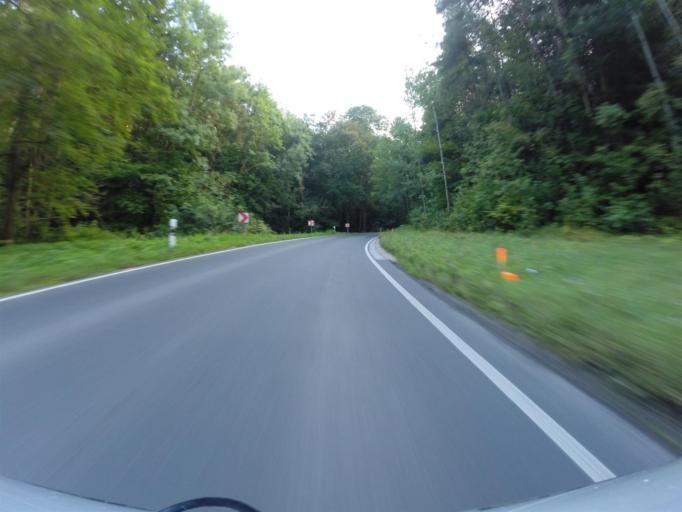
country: DE
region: Thuringia
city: Bucha
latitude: 50.8843
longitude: 11.5406
